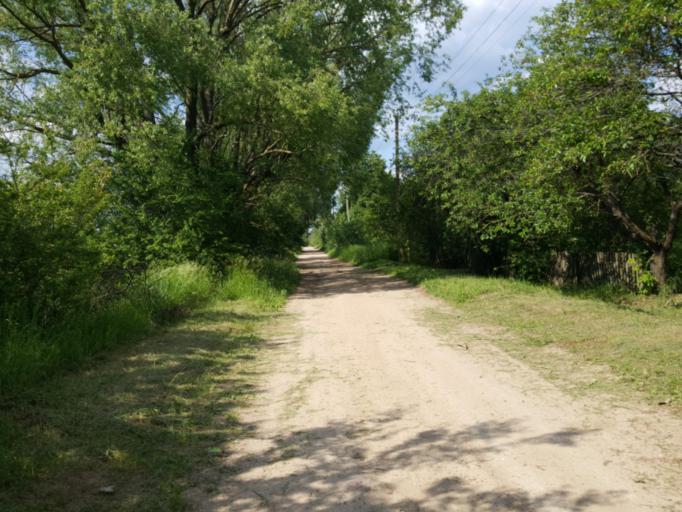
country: BY
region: Brest
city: Vysokaye
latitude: 52.4470
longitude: 23.5804
